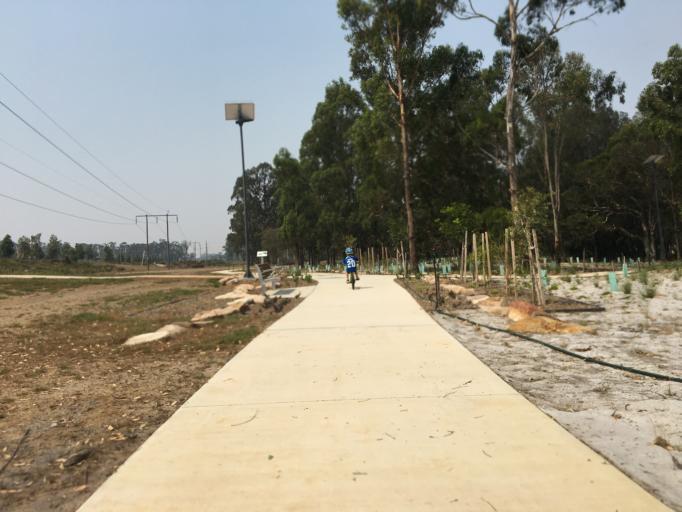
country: AU
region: New South Wales
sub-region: Campbelltown Municipality
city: Denham Court
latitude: -33.9759
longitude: 150.8146
